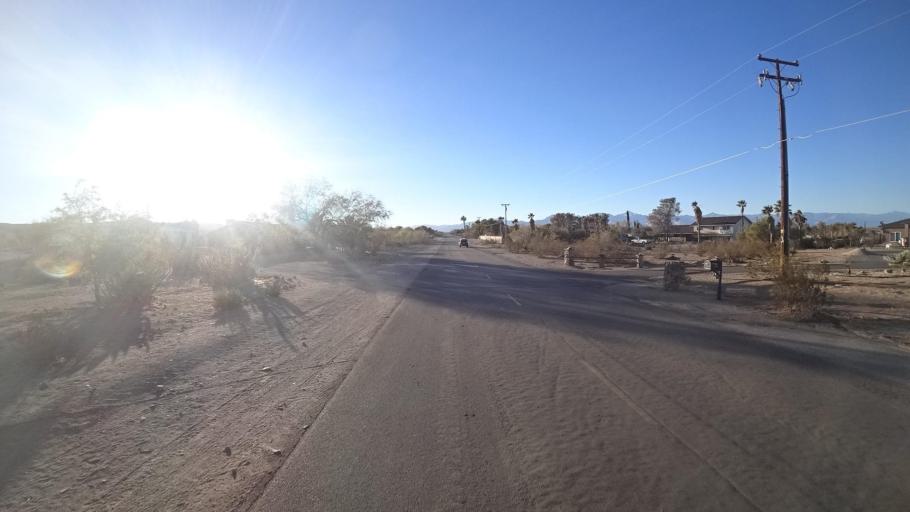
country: US
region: California
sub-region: Kern County
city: Ridgecrest
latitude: 35.5862
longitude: -117.6552
